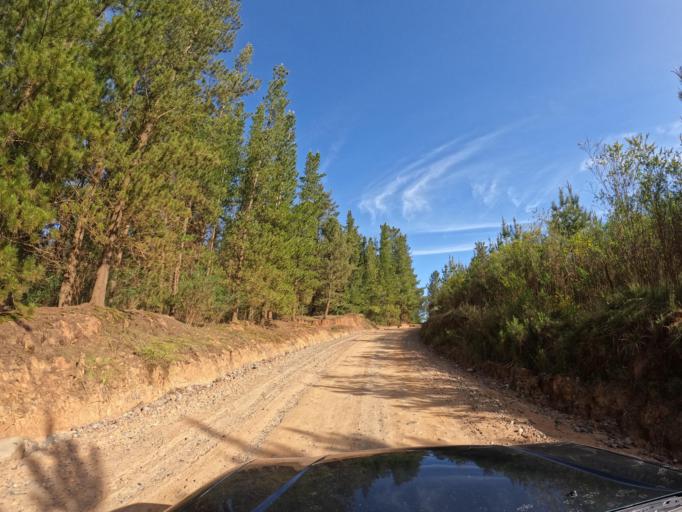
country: CL
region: Biobio
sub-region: Provincia de Biobio
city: Yumbel
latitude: -37.1043
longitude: -72.7415
